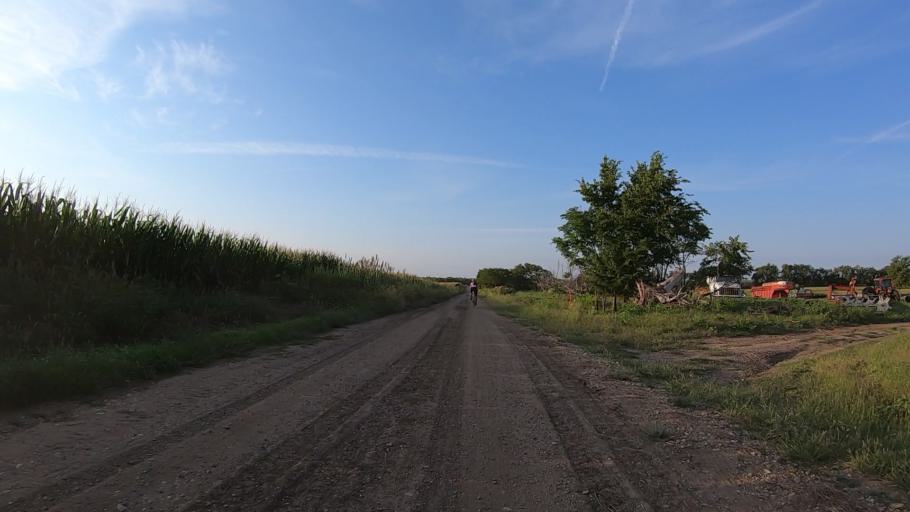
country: US
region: Kansas
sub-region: Marshall County
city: Blue Rapids
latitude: 39.7676
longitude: -96.7508
